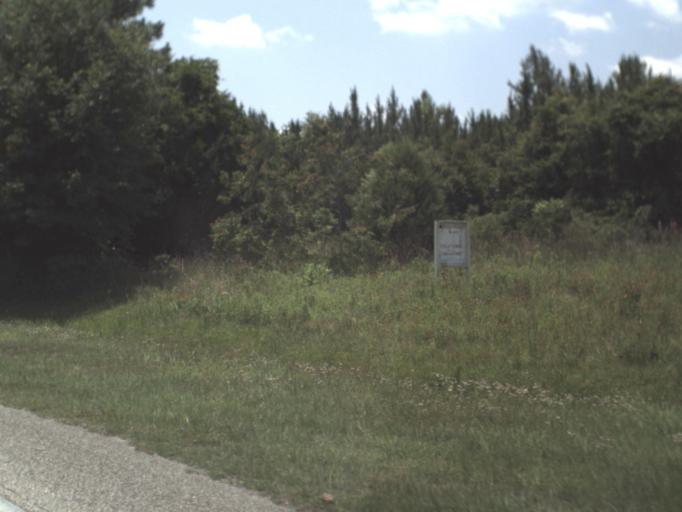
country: US
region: Florida
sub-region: Bradford County
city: Starke
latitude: 29.8770
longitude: -82.1509
